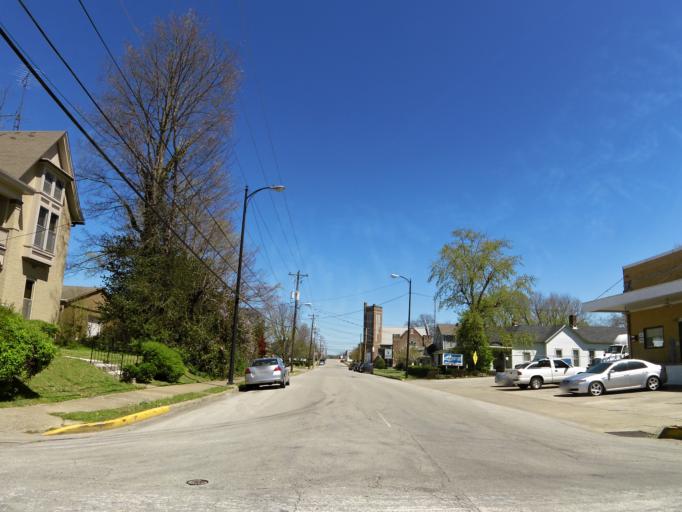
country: US
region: Kentucky
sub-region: Warren County
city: Bowling Green
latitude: 36.9961
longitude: -86.4356
